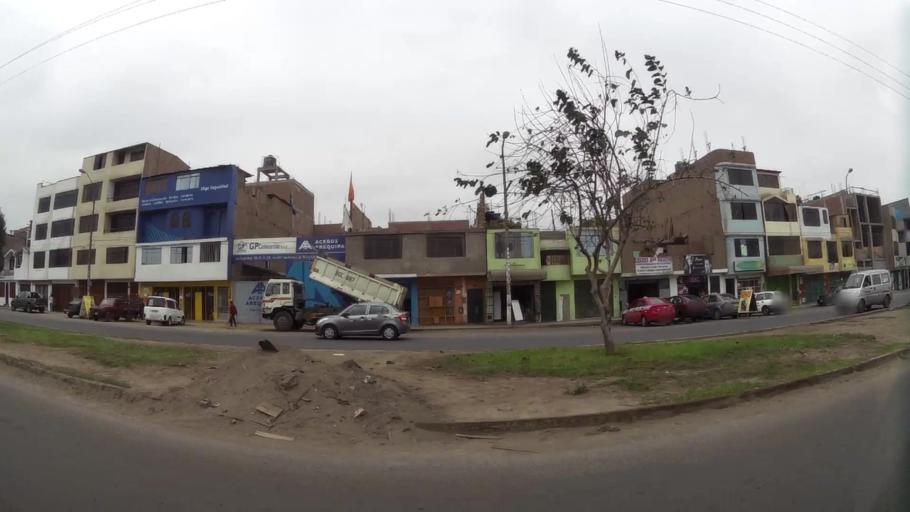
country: PE
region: Lima
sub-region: Lima
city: Independencia
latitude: -11.9798
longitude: -77.0848
